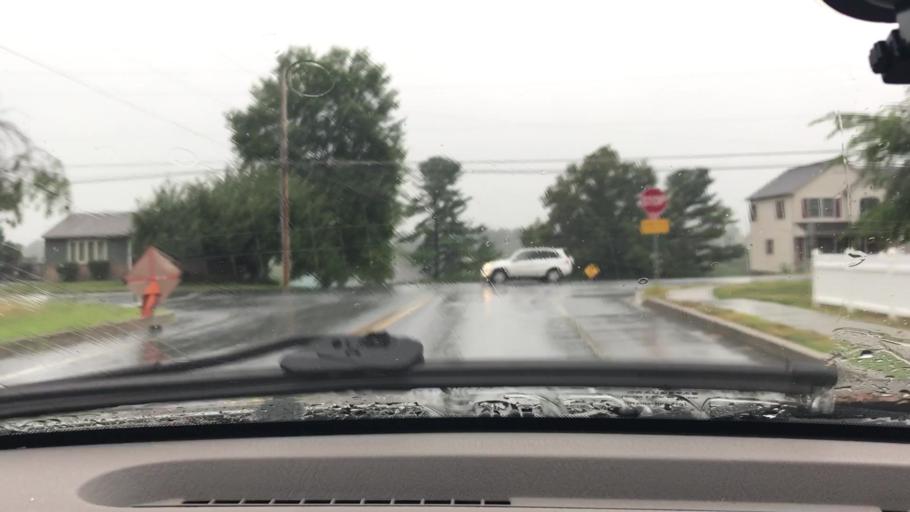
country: US
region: Pennsylvania
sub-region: Lancaster County
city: Elizabethtown
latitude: 40.1284
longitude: -76.6119
